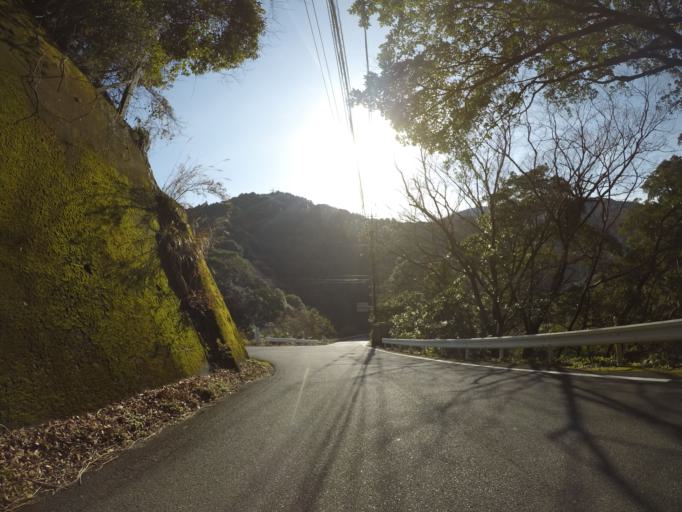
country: JP
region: Shizuoka
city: Heda
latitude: 34.8077
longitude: 138.8235
